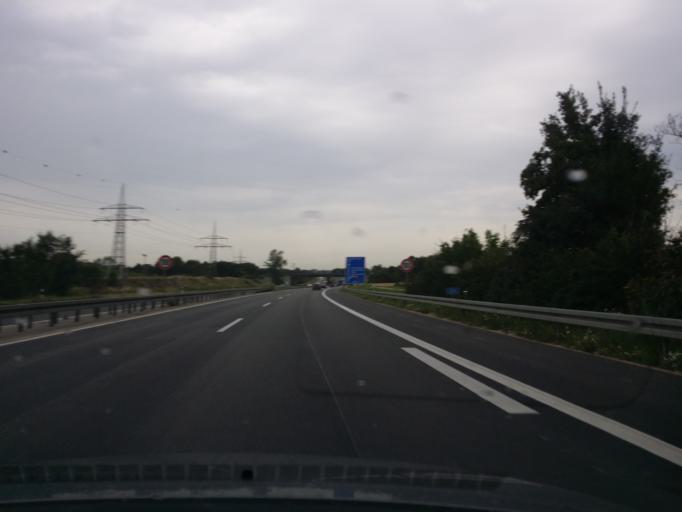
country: DE
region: Hesse
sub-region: Regierungsbezirk Darmstadt
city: Ginsheim-Gustavsburg
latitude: 49.9904
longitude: 8.3405
